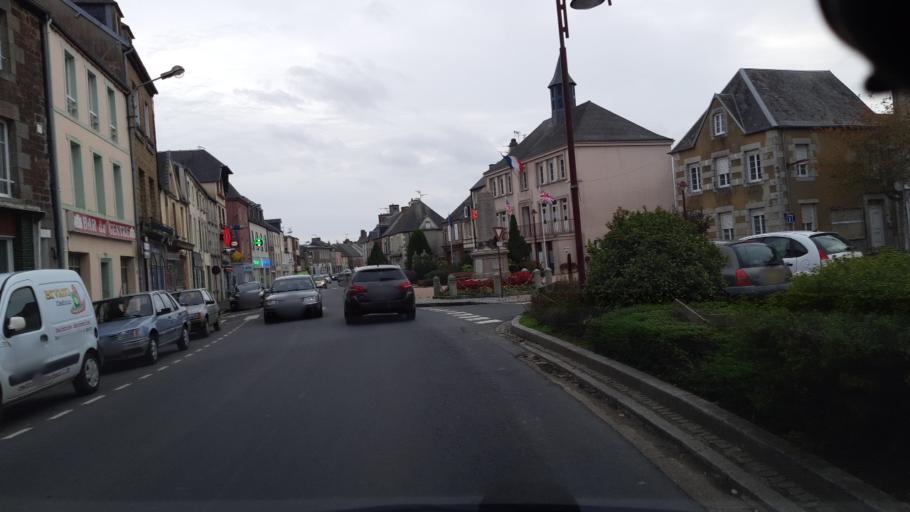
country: FR
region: Lower Normandy
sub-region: Departement de la Manche
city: Quettreville-sur-Sienne
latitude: 48.9168
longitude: -1.4353
